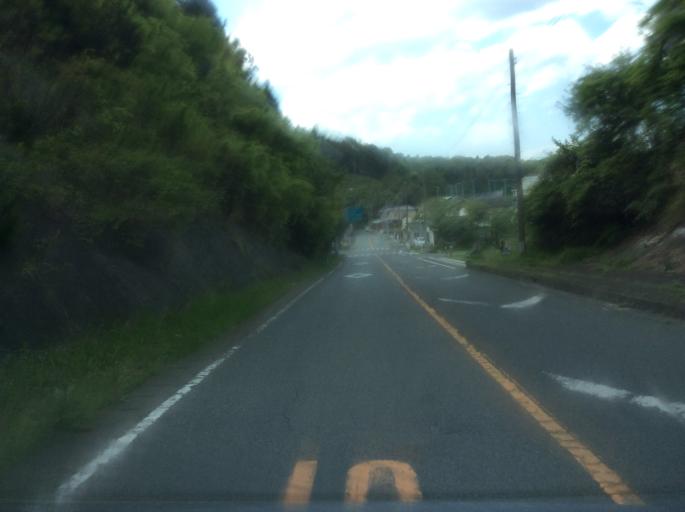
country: JP
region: Ibaraki
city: Kitaibaraki
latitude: 36.8787
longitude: 140.7864
